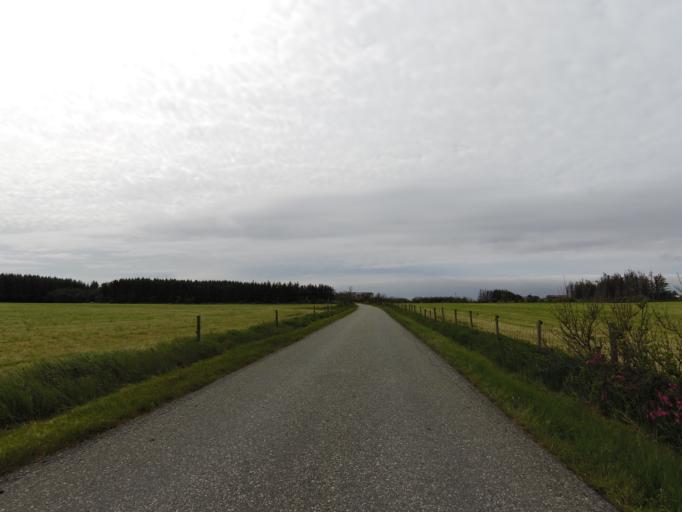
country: NO
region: Rogaland
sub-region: Ha
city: Naerbo
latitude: 58.6377
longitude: 5.6056
